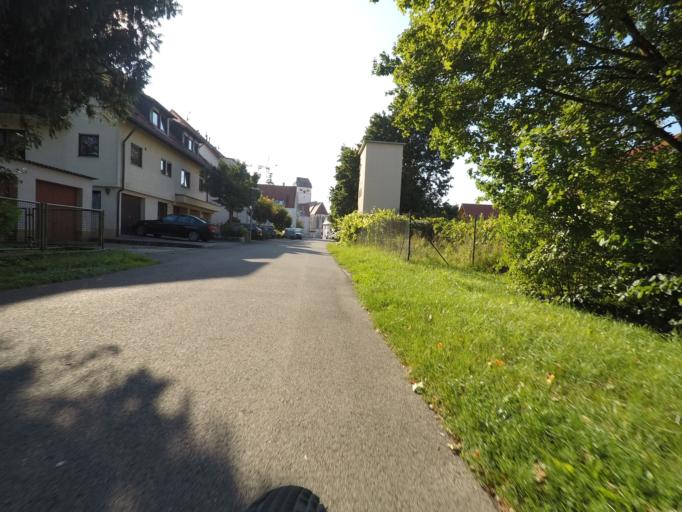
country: DE
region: Baden-Wuerttemberg
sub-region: Regierungsbezirk Stuttgart
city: Ehningen
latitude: 48.6914
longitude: 8.9539
